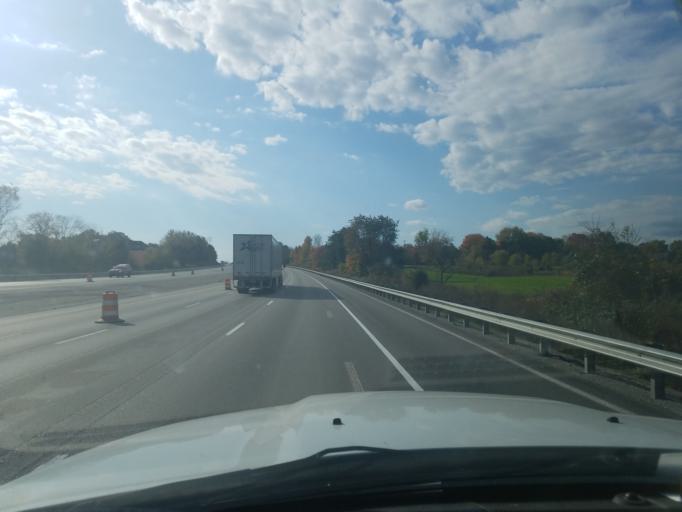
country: US
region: Indiana
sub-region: Clark County
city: Sellersburg
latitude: 38.4588
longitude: -85.7709
